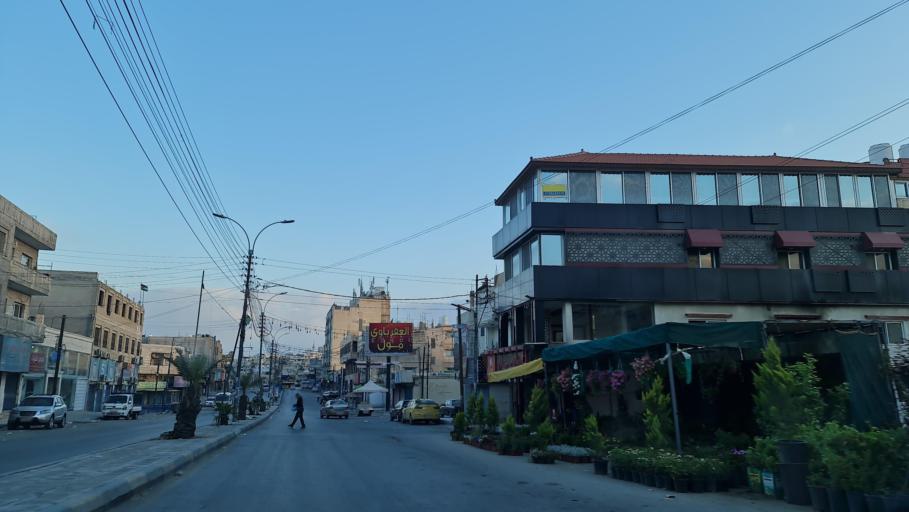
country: JO
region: Zarqa
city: Zarqa
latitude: 32.0765
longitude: 36.0767
